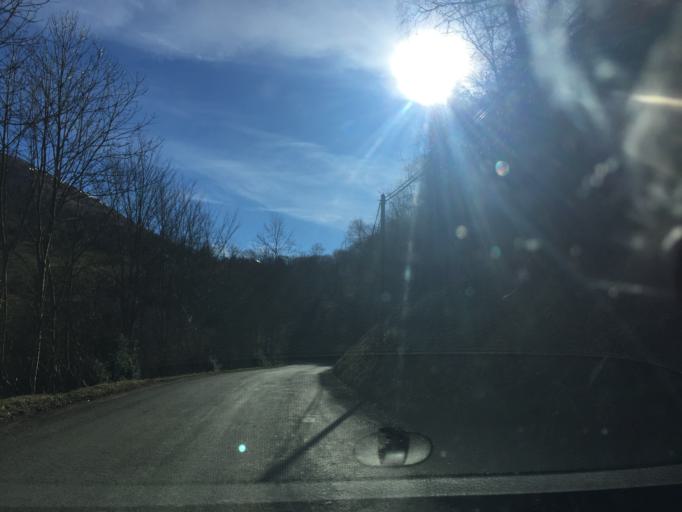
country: FR
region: Midi-Pyrenees
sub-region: Departement des Hautes-Pyrenees
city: Saint-Lary-Soulan
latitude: 42.8170
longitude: 0.3417
